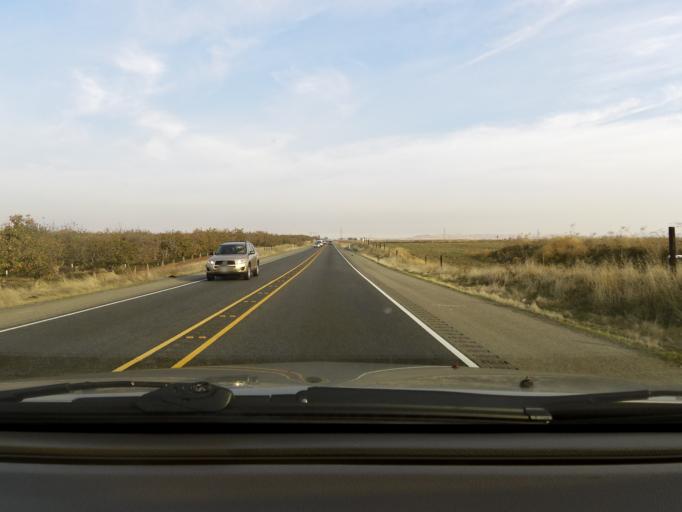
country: US
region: California
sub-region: Madera County
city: Bonadelle Ranchos-Madera Ranchos
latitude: 36.9283
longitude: -119.7940
